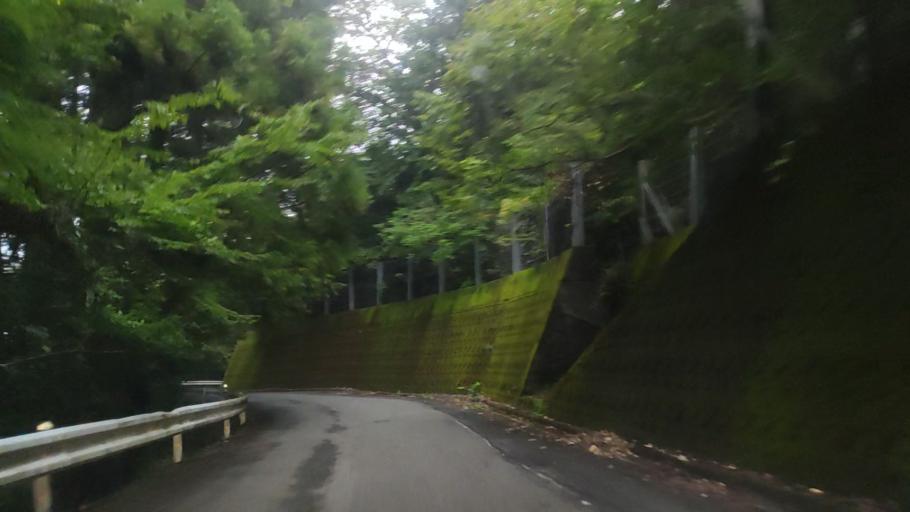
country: JP
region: Wakayama
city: Hashimoto
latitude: 34.2952
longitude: 135.6284
